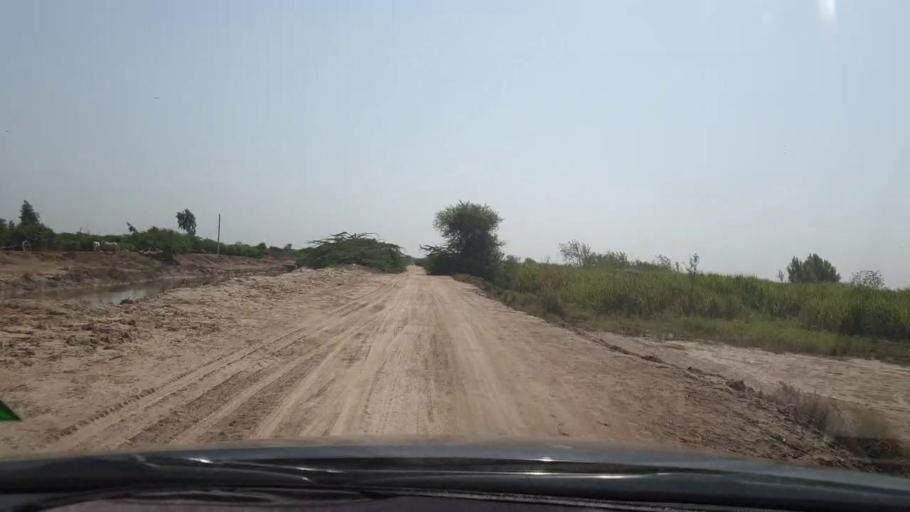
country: PK
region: Sindh
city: Tando Bago
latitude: 24.7922
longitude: 69.1130
